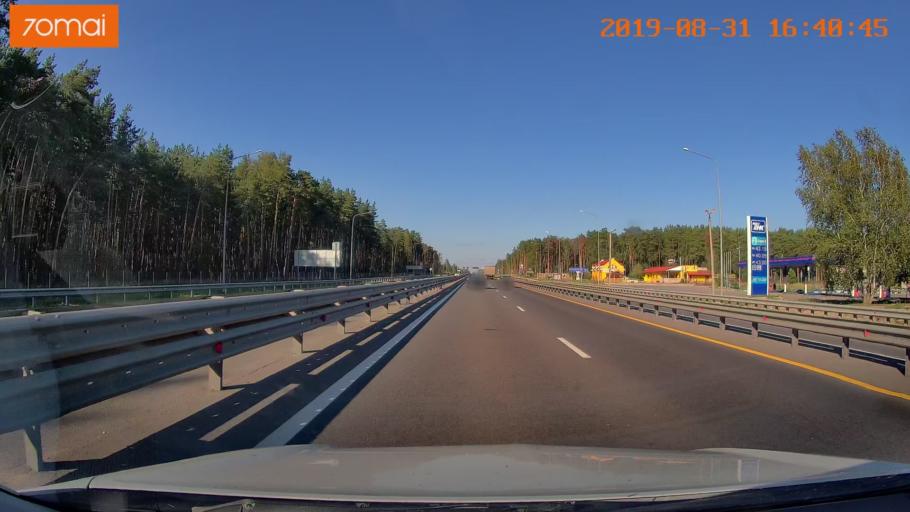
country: RU
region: Kaluga
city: Kurovskoye
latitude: 54.5700
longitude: 36.0546
